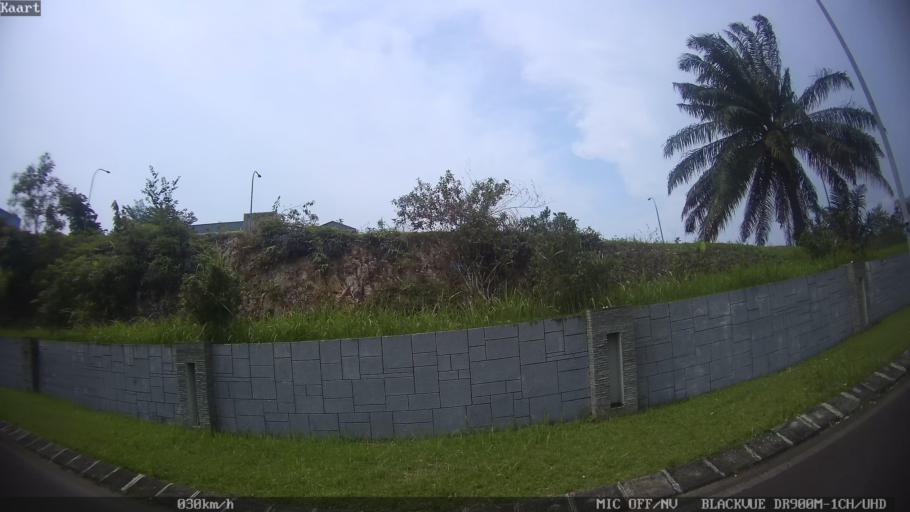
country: ID
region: Lampung
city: Bandarlampung
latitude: -5.4301
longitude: 105.2811
